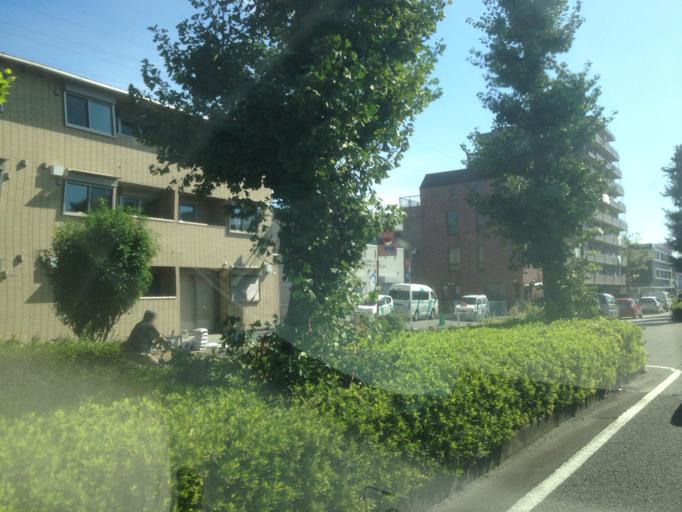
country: JP
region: Tokyo
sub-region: Machida-shi
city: Machida
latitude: 35.5681
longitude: 139.3845
